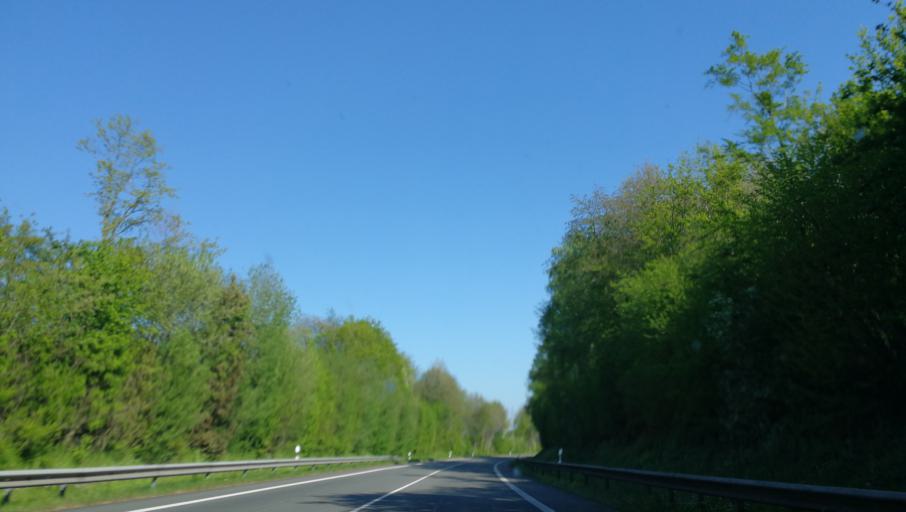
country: DE
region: North Rhine-Westphalia
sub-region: Regierungsbezirk Munster
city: Dreierwalde
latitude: 52.2409
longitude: 7.4846
